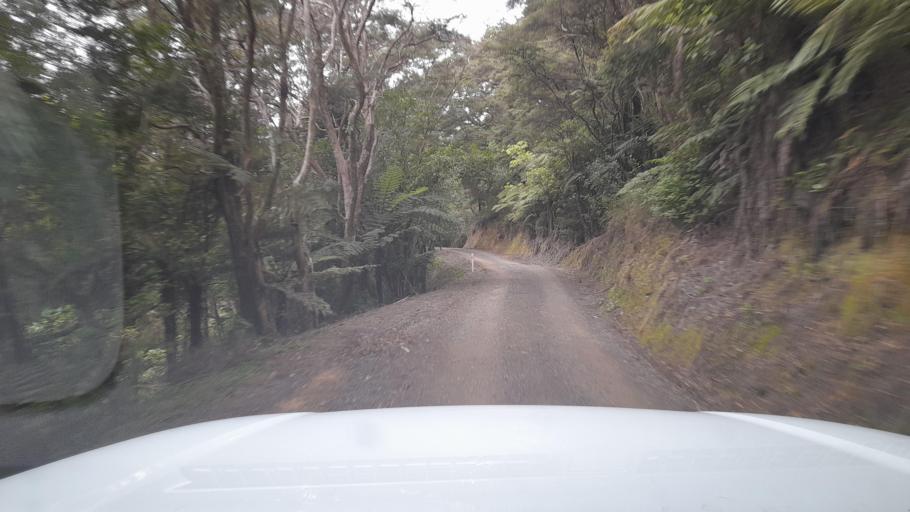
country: NZ
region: Northland
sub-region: Far North District
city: Paihia
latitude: -35.3576
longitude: 174.2367
